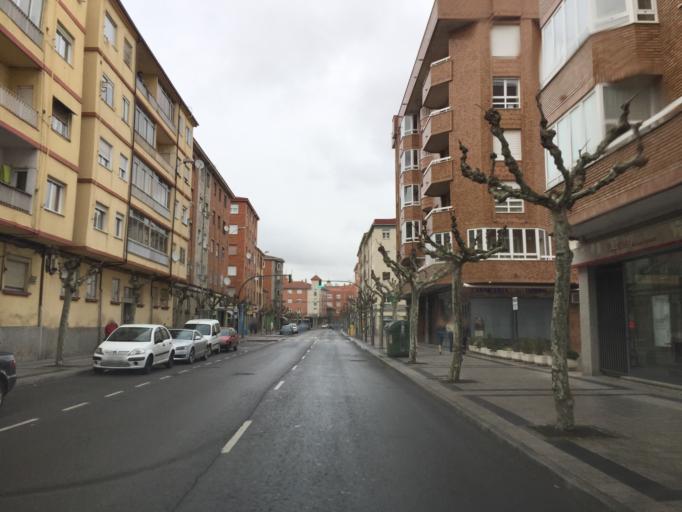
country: ES
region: Castille and Leon
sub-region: Provincia de Leon
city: Leon
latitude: 42.6153
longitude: -5.5687
